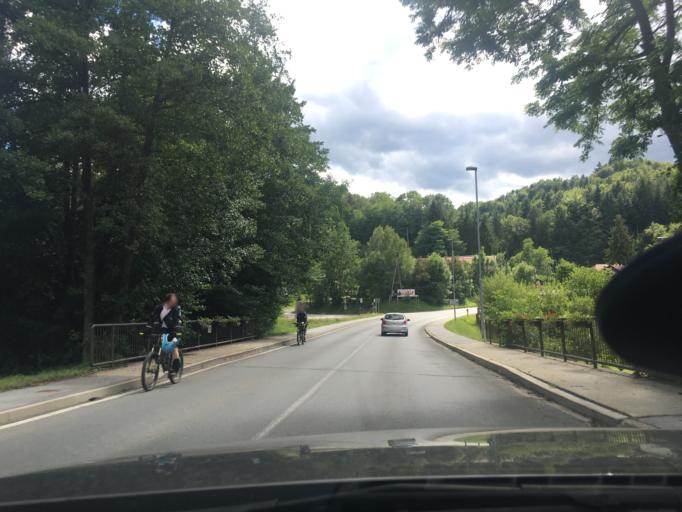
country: SI
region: Ruse
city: Bistrica ob Dravi
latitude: 46.5537
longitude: 15.5509
